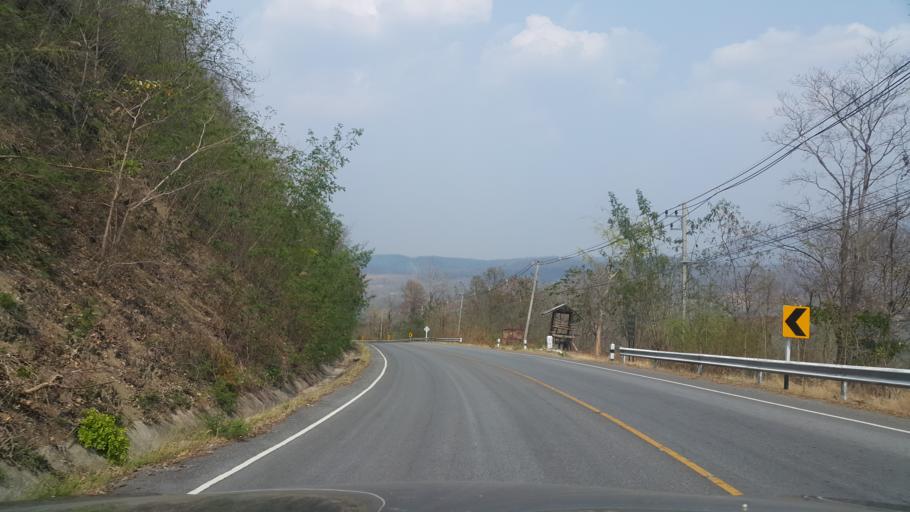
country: TH
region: Lamphun
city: Thung Hua Chang
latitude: 17.9075
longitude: 99.1483
